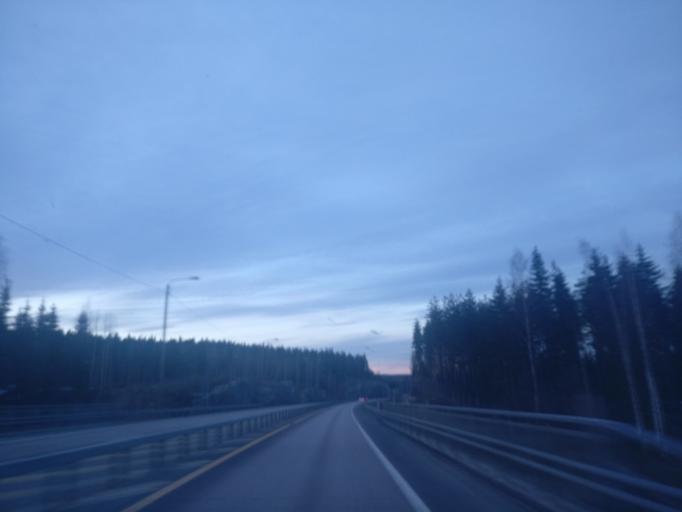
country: FI
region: Central Finland
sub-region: Jyvaeskylae
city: Saeynaetsalo
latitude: 62.2118
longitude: 25.8897
